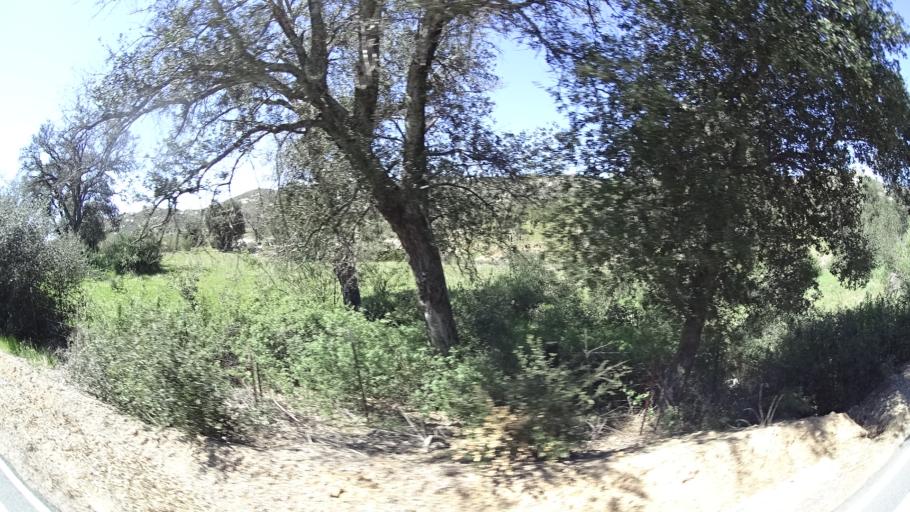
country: US
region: California
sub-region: San Diego County
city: Descanso
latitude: 32.8704
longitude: -116.5896
